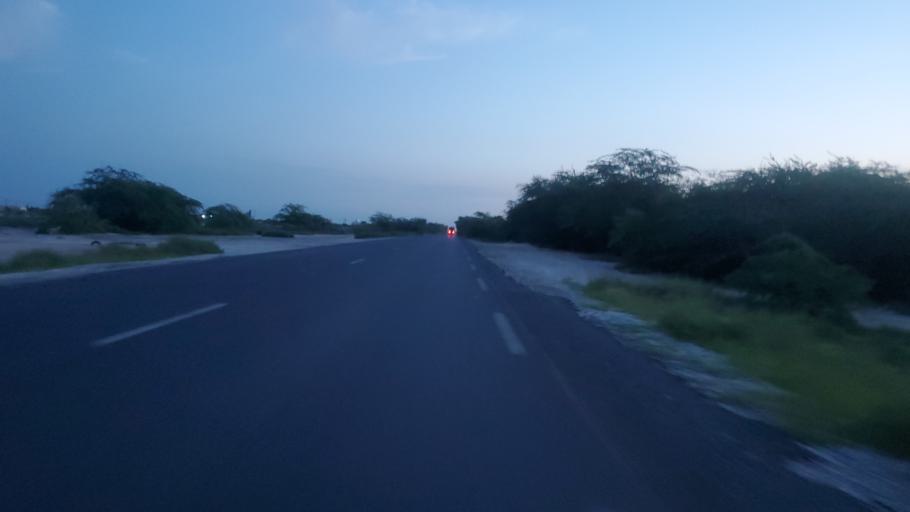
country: SN
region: Saint-Louis
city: Saint-Louis
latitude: 16.0647
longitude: -16.3937
